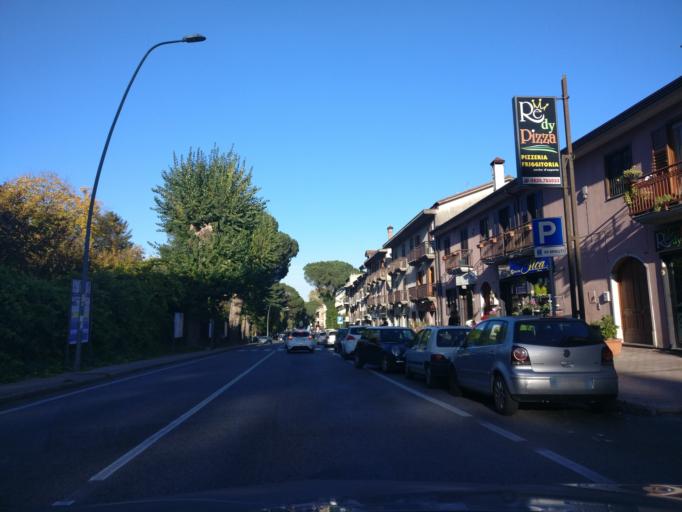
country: IT
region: Campania
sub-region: Provincia di Avellino
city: Torelli-Torrette
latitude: 40.9088
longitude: 14.7672
